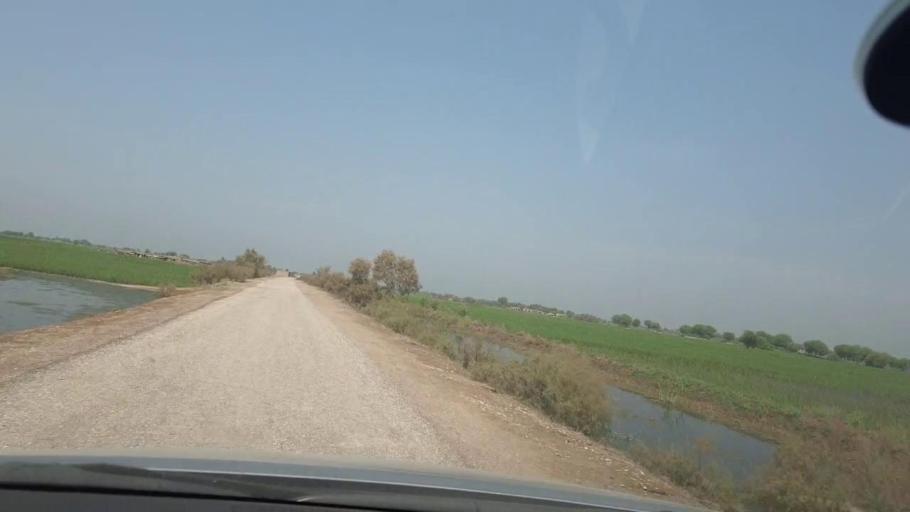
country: PK
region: Balochistan
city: Mehrabpur
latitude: 28.0692
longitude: 68.0541
